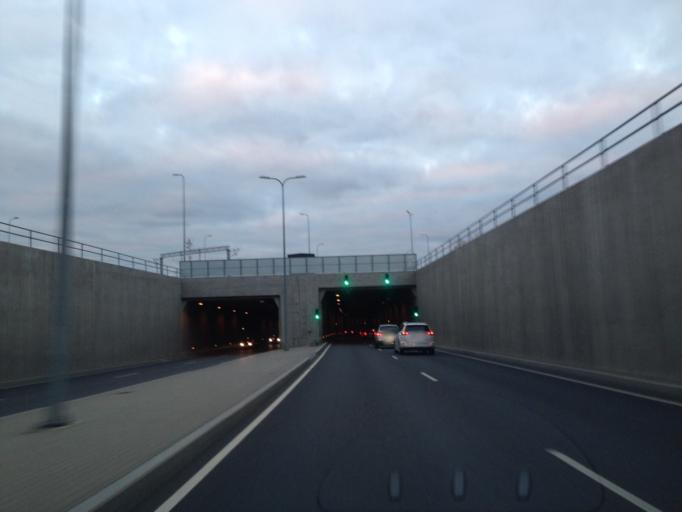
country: EE
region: Harju
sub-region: Tallinna linn
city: Tallinn
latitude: 59.4189
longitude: 24.7666
